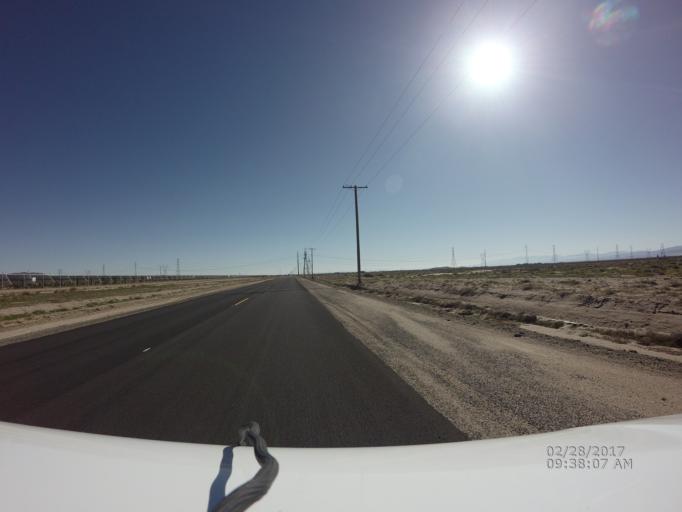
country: US
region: California
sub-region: Kern County
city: Rosamond
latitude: 34.8194
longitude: -118.3483
